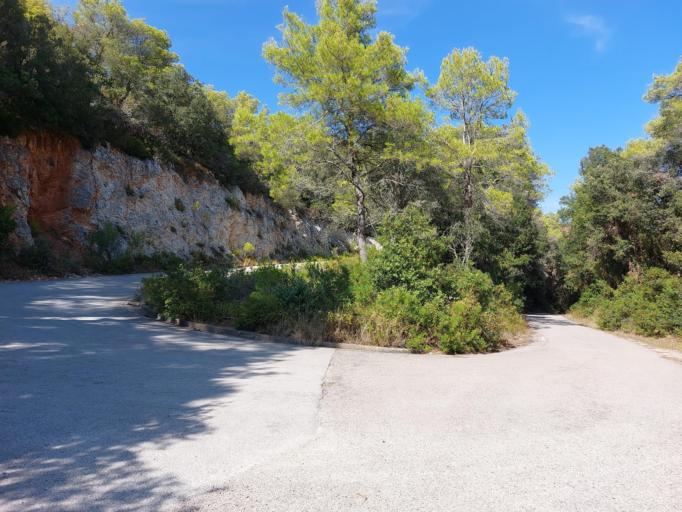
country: HR
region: Dubrovacko-Neretvanska
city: Smokvica
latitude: 42.7411
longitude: 16.8247
